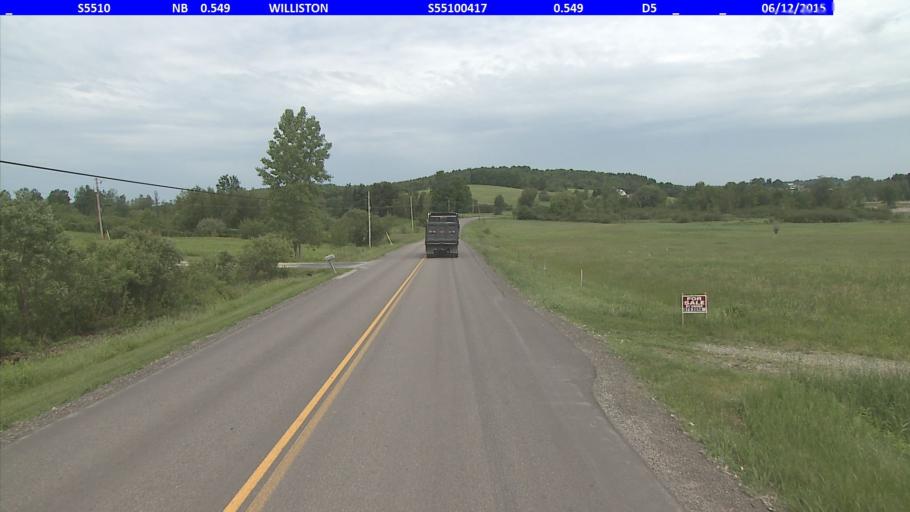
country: US
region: Vermont
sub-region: Chittenden County
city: Hinesburg
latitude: 44.3804
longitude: -73.0967
